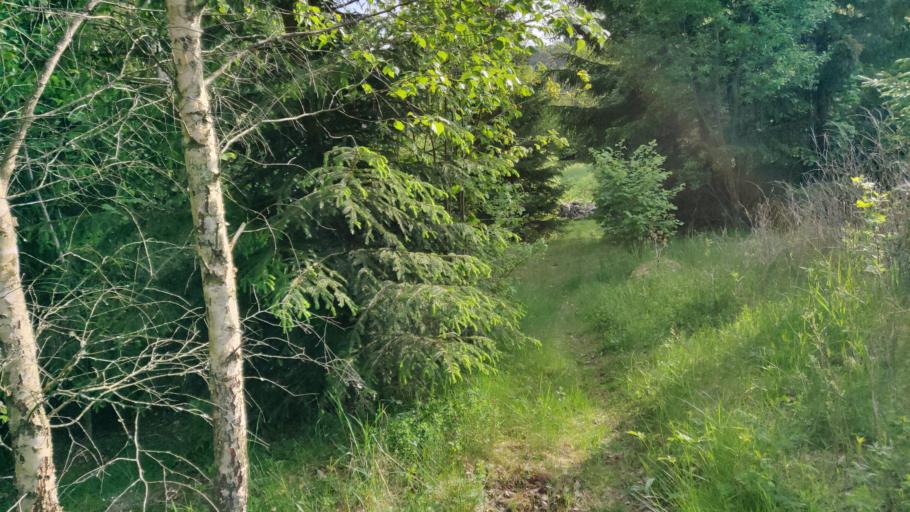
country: SE
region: Vaestra Goetaland
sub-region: Ulricehamns Kommun
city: Ulricehamn
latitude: 57.7828
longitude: 13.3696
